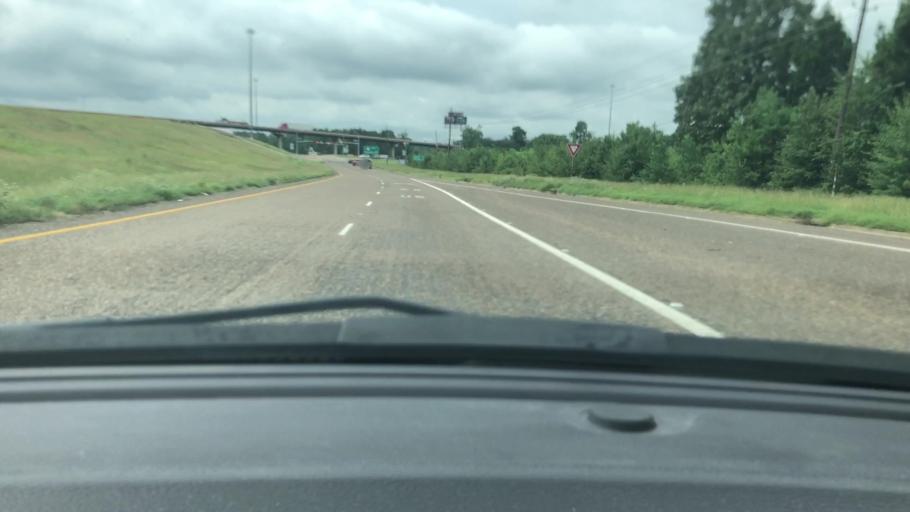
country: US
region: Texas
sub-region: Bowie County
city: Wake Village
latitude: 33.3976
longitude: -94.0985
